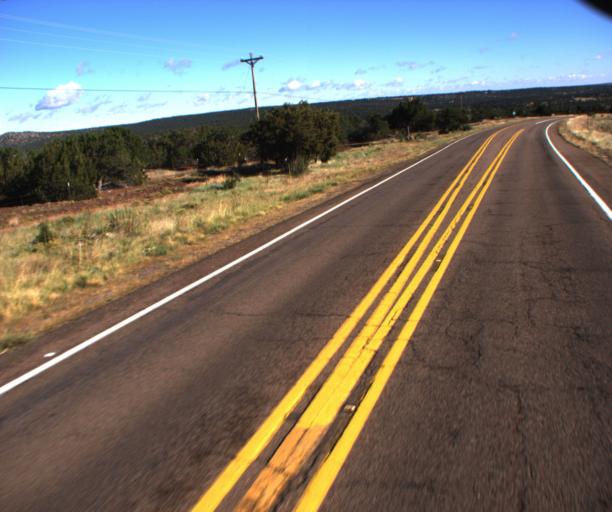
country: US
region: Arizona
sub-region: Navajo County
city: White Mountain Lake
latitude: 34.3151
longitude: -109.7673
